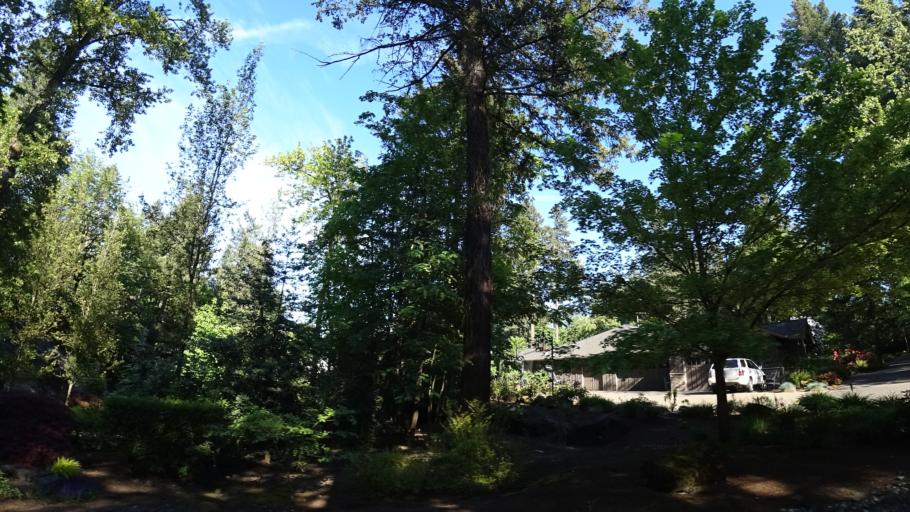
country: US
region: Oregon
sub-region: Washington County
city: Raleigh Hills
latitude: 45.4894
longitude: -122.7528
